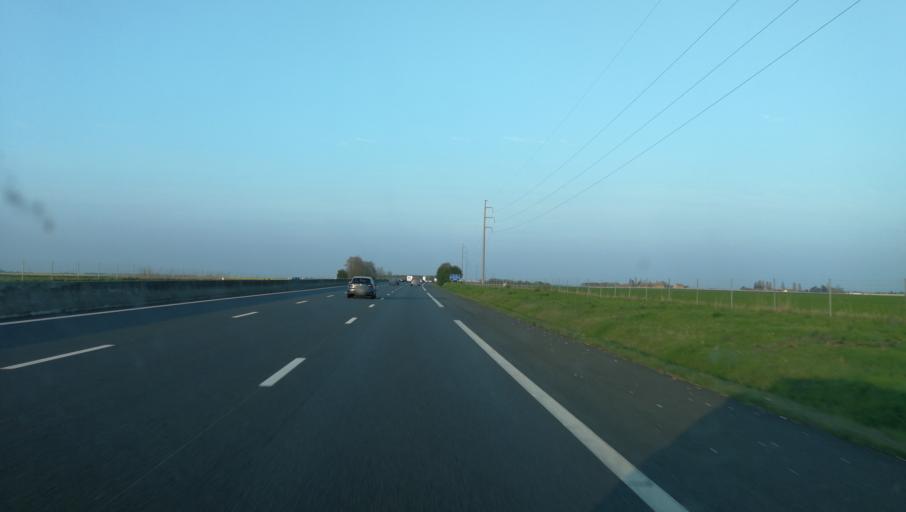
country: FR
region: Centre
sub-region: Departement d'Eure-et-Loir
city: Bailleau-le-Pin
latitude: 48.3149
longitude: 1.3253
